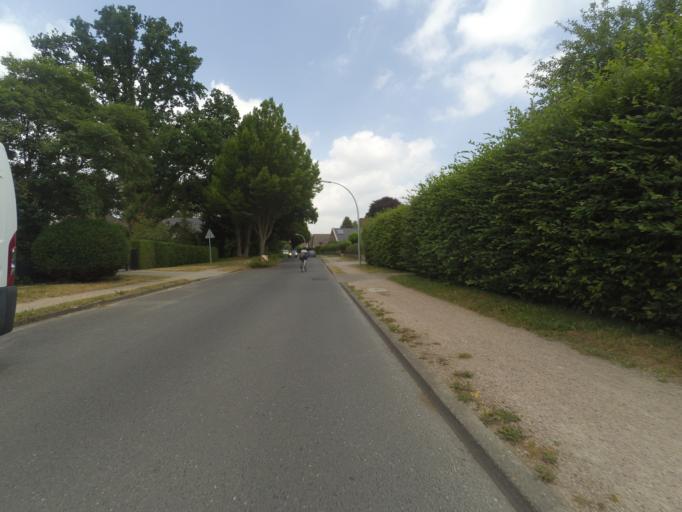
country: DE
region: Hamburg
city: Sasel
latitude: 53.6394
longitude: 10.1236
